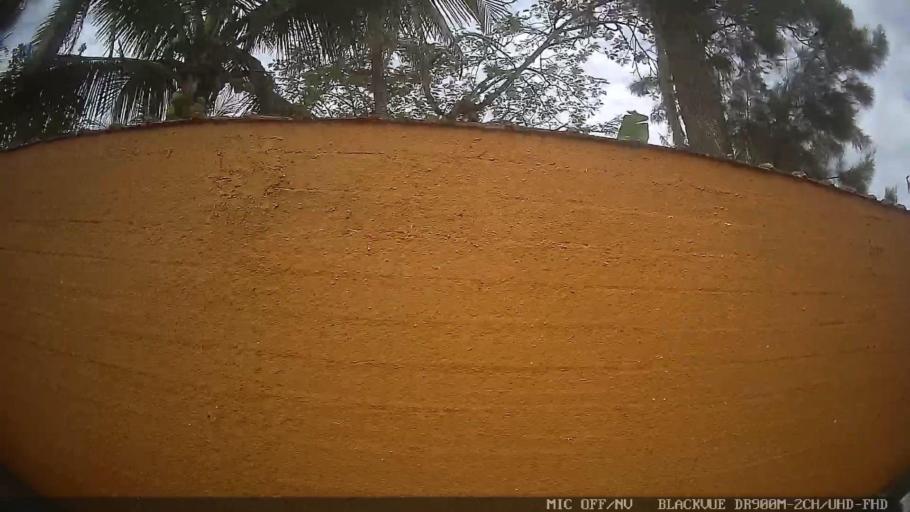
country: BR
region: Sao Paulo
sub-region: Sao Sebastiao
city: Sao Sebastiao
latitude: -23.6952
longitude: -45.4387
